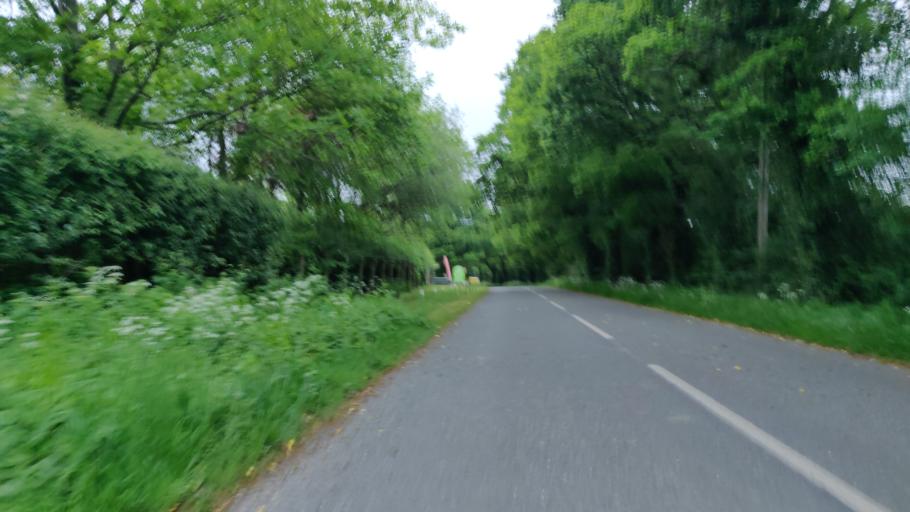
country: GB
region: England
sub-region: West Sussex
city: Partridge Green
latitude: 50.9885
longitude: -0.3039
